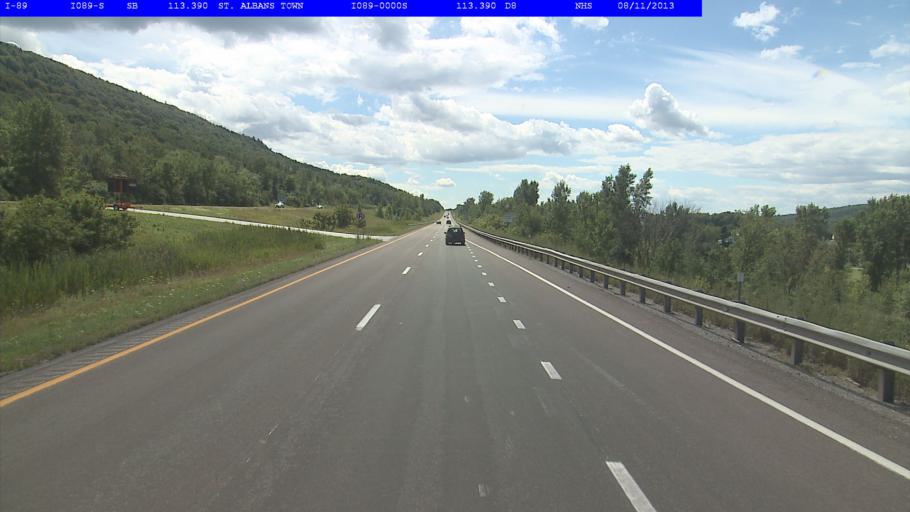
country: US
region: Vermont
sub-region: Franklin County
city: Saint Albans
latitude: 44.7900
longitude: -73.0720
